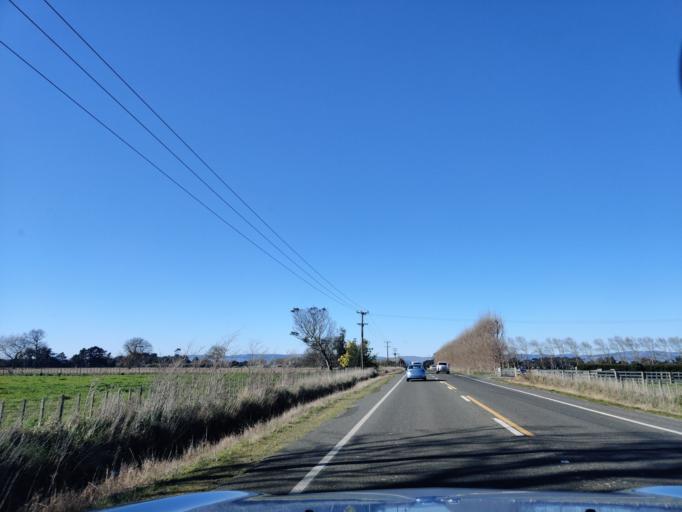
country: NZ
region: Manawatu-Wanganui
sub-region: Palmerston North City
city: Palmerston North
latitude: -40.2985
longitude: 175.5767
